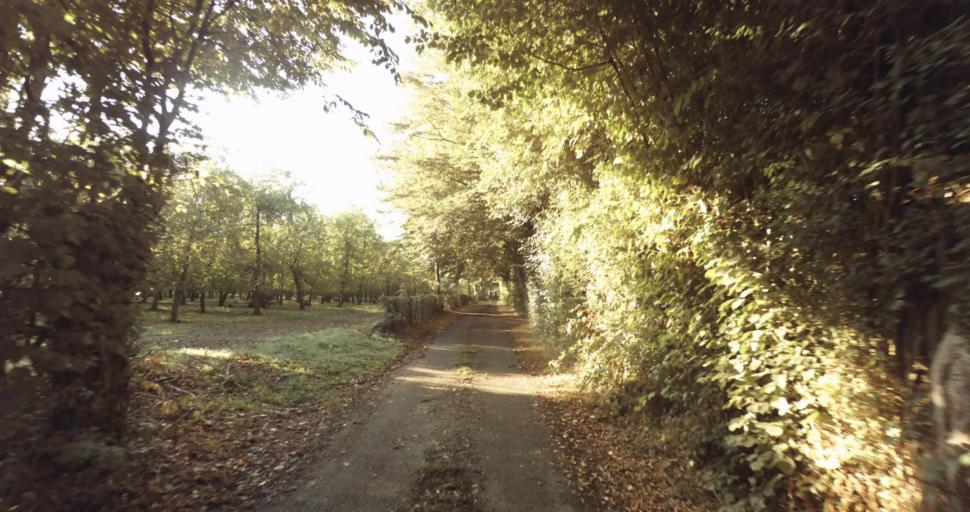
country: FR
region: Lower Normandy
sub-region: Departement de l'Orne
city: Vimoutiers
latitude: 48.9136
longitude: 0.1568
